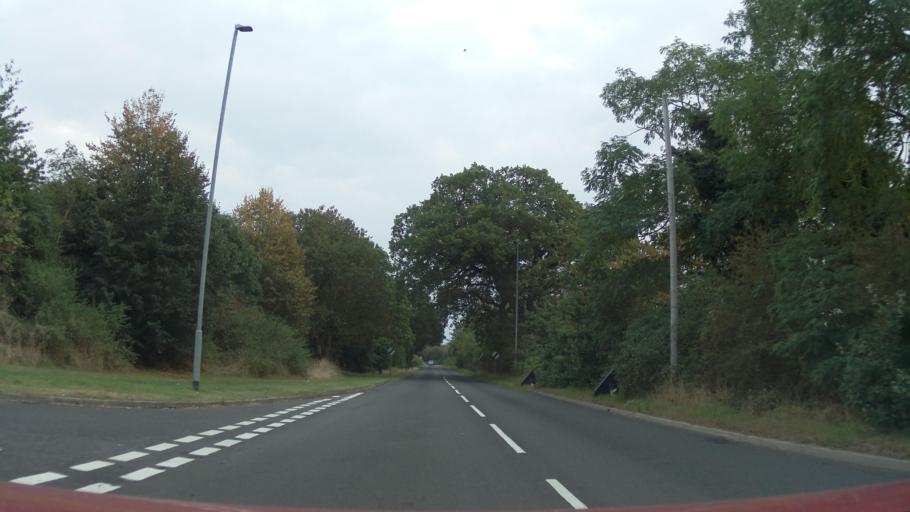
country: GB
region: England
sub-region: Nottinghamshire
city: South Collingham
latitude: 53.1461
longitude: -0.6689
